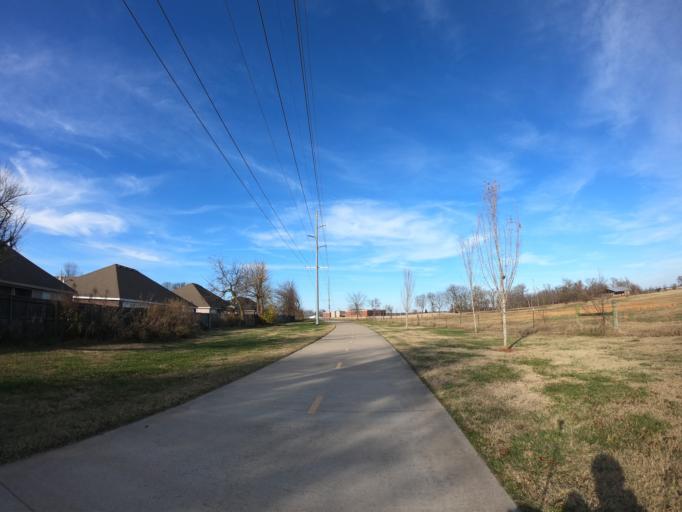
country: US
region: Arkansas
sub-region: Benton County
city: Lowell
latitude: 36.2755
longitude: -94.1675
